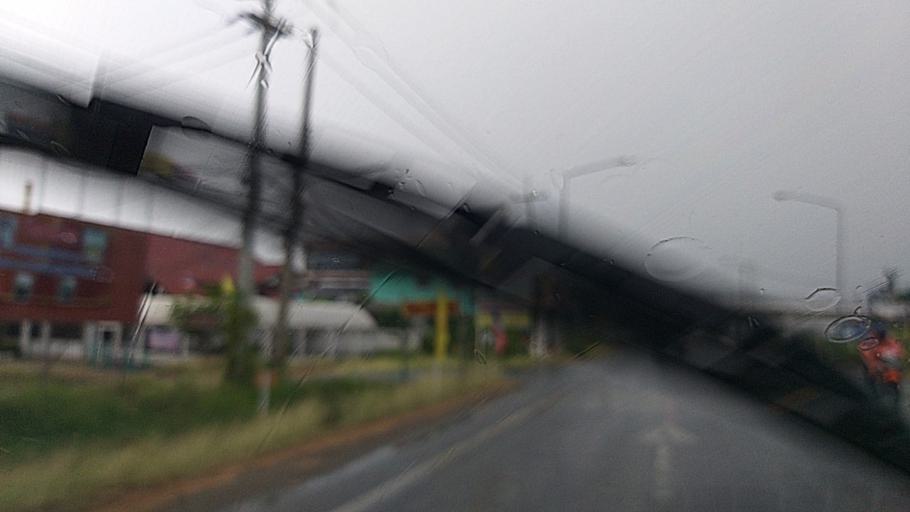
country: TH
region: Phra Nakhon Si Ayutthaya
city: Phra Nakhon Si Ayutthaya
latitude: 14.3508
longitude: 100.5837
